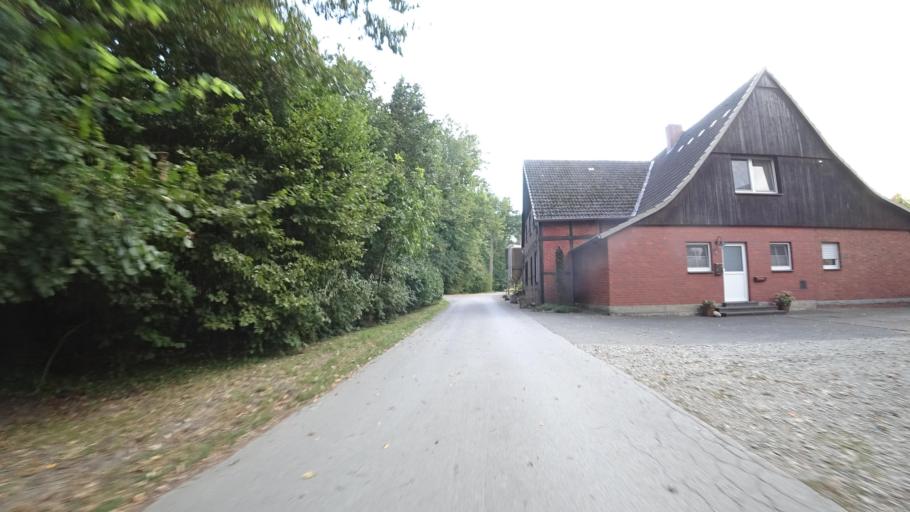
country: DE
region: North Rhine-Westphalia
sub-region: Regierungsbezirk Detmold
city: Rheda-Wiedenbruck
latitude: 51.8332
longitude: 8.2743
